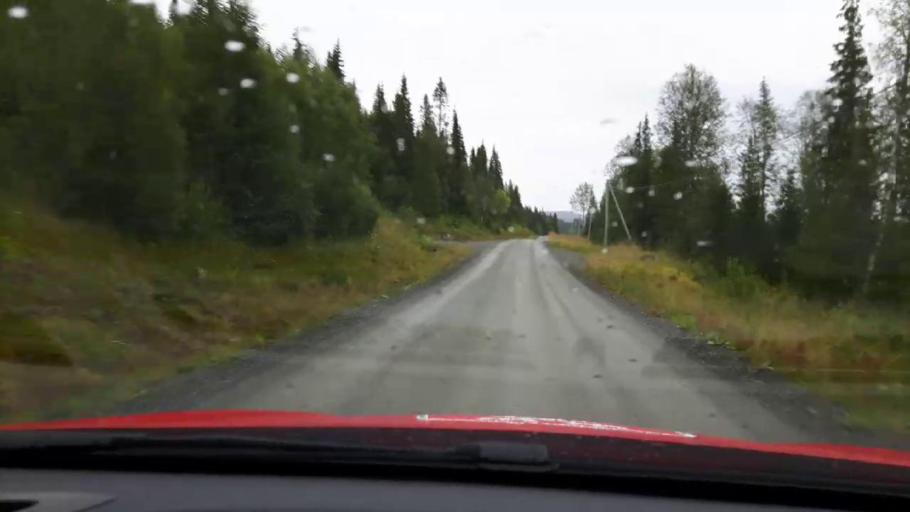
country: SE
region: Jaemtland
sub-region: Are Kommun
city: Are
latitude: 63.5058
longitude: 12.7404
